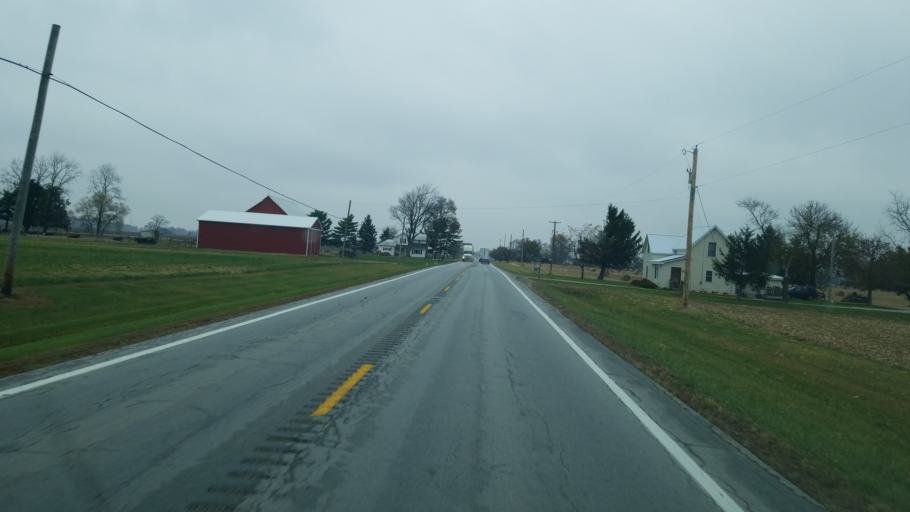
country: US
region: Ohio
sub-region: Union County
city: Marysville
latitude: 40.3245
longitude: -83.3208
